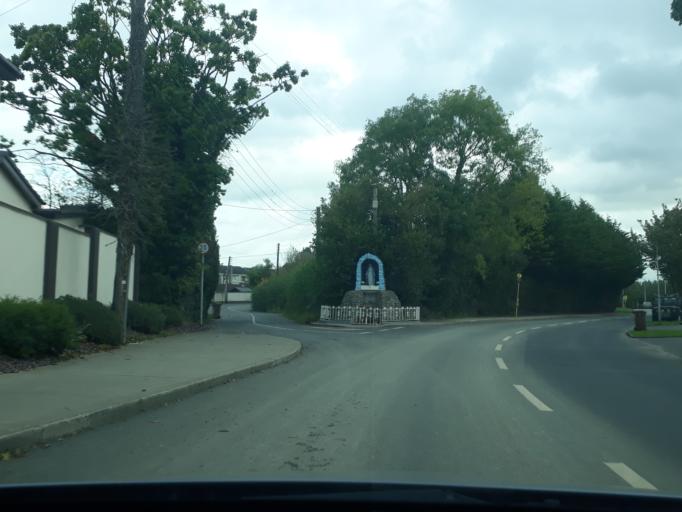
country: IE
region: Leinster
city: Lucan
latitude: 53.3503
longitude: -6.4646
